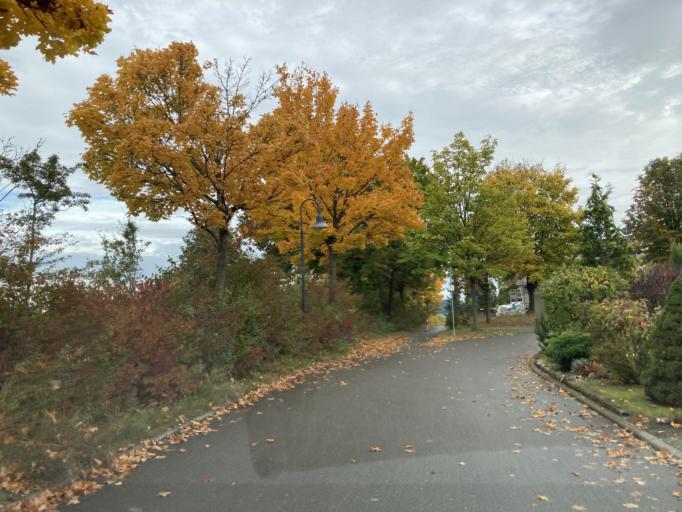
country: DE
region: Baden-Wuerttemberg
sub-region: Regierungsbezirk Stuttgart
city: Bondorf
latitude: 48.5068
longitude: 8.8844
